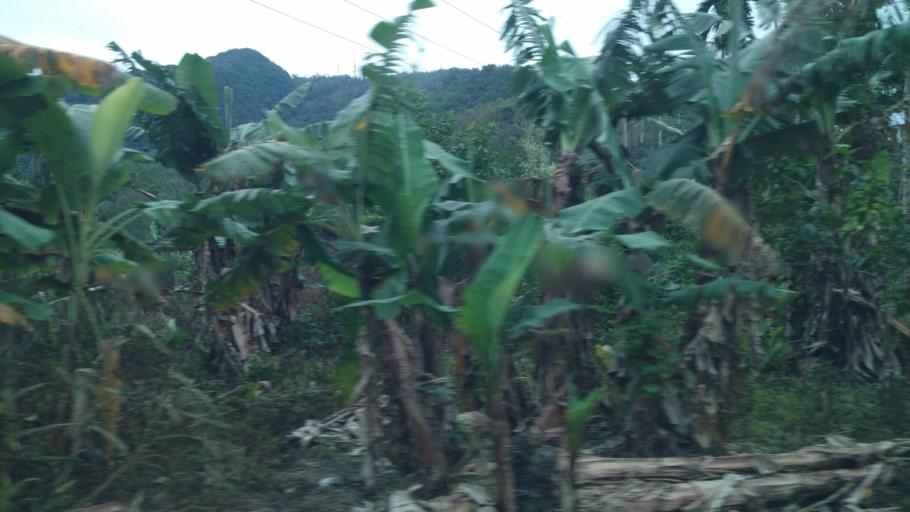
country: TW
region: Taiwan
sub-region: Hualien
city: Hualian
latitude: 23.9234
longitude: 121.5052
